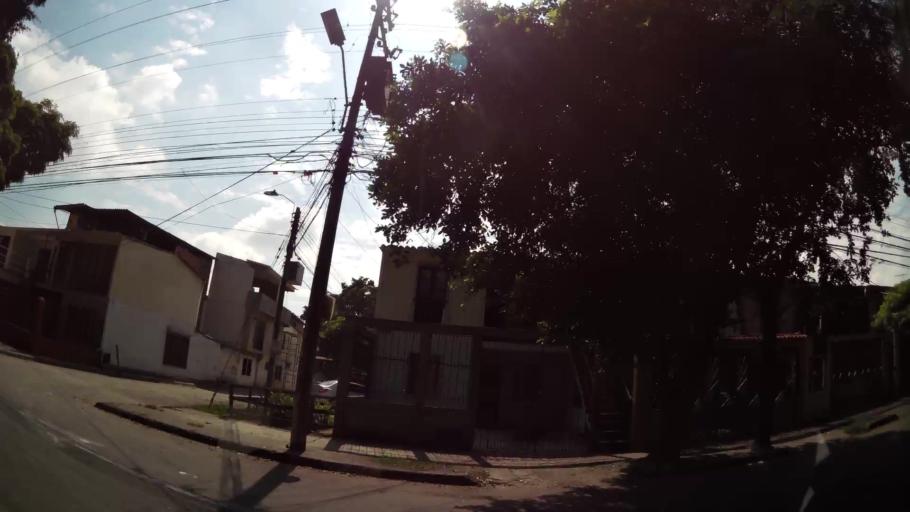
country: CO
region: Valle del Cauca
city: Cali
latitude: 3.4924
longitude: -76.4998
